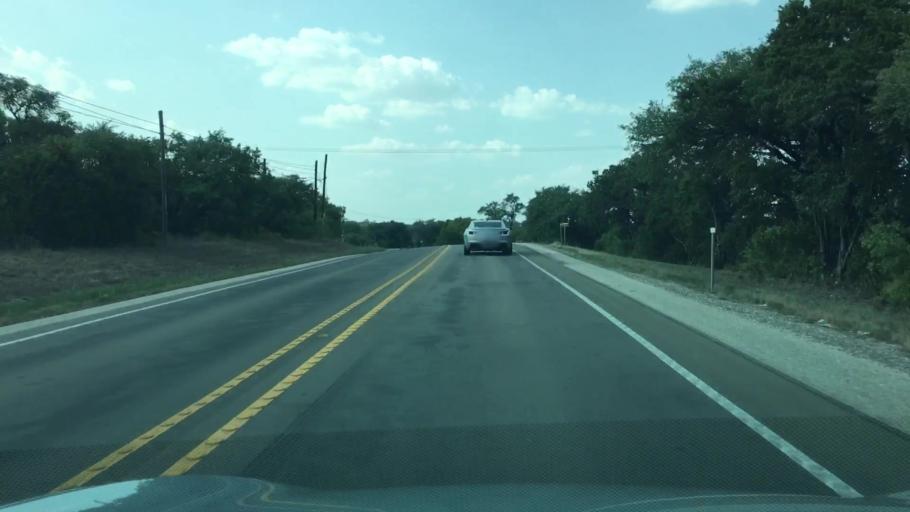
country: US
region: Texas
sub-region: Hays County
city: Dripping Springs
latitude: 30.1212
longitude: -98.0886
